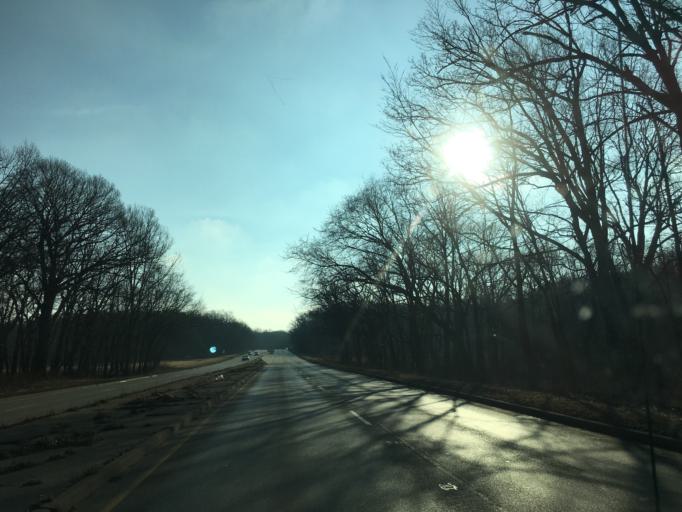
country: US
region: Illinois
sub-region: Cook County
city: Elk Grove Village
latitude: 42.0302
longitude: -88.0026
